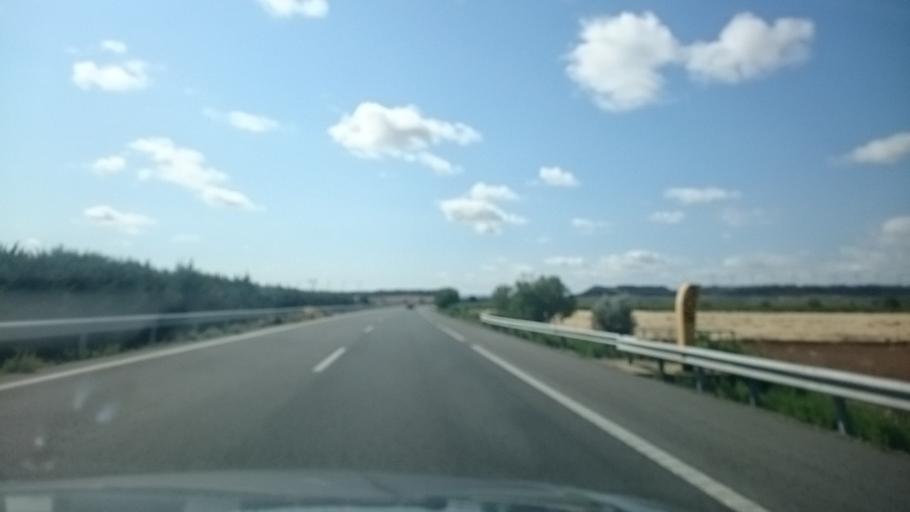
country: ES
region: Navarre
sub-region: Provincia de Navarra
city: Corella
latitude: 42.1107
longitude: -1.7330
